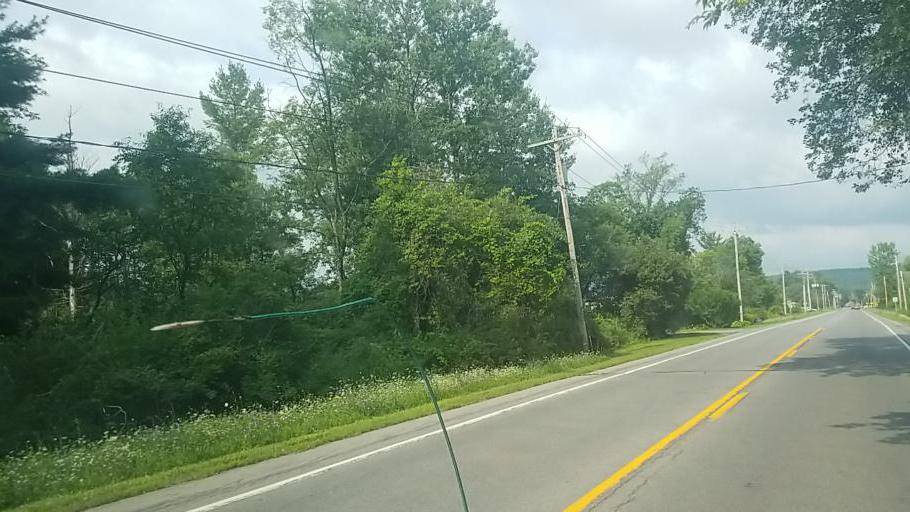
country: US
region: New York
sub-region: Fulton County
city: Gloversville
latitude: 43.0533
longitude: -74.3713
